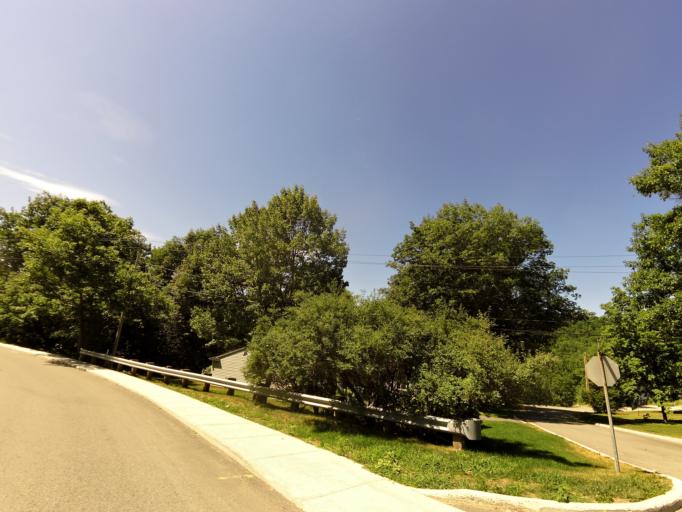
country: CA
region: Quebec
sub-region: Abitibi-Temiscamingue
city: Temiscaming
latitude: 46.7181
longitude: -79.1027
